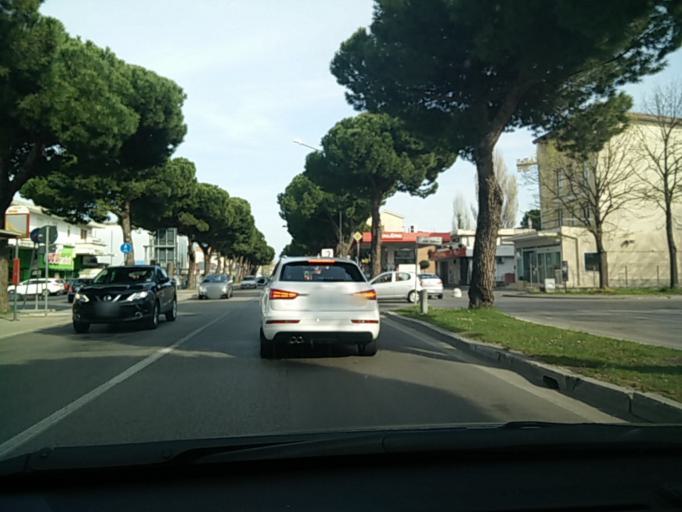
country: IT
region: Emilia-Romagna
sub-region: Provincia di Rimini
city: Rimini
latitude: 44.0687
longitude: 12.5504
